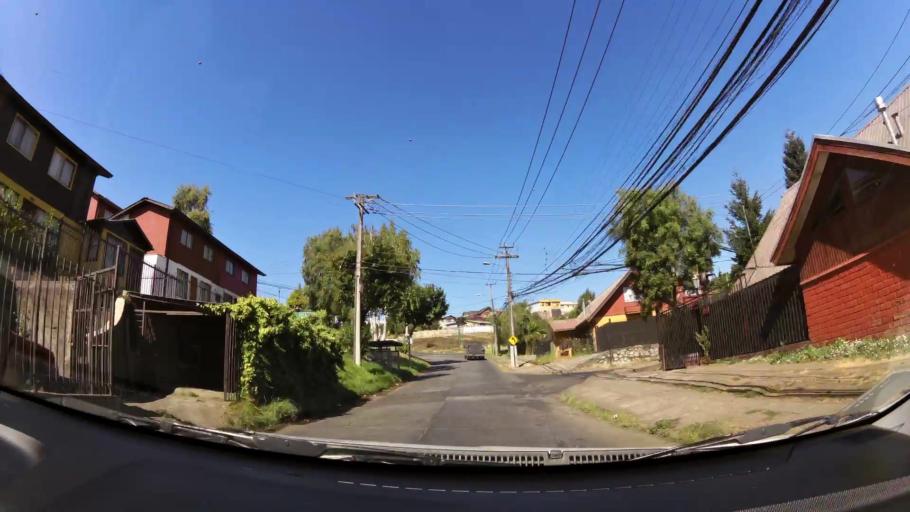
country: CL
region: Biobio
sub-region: Provincia de Concepcion
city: Concepcion
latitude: -36.7944
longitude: -73.0497
